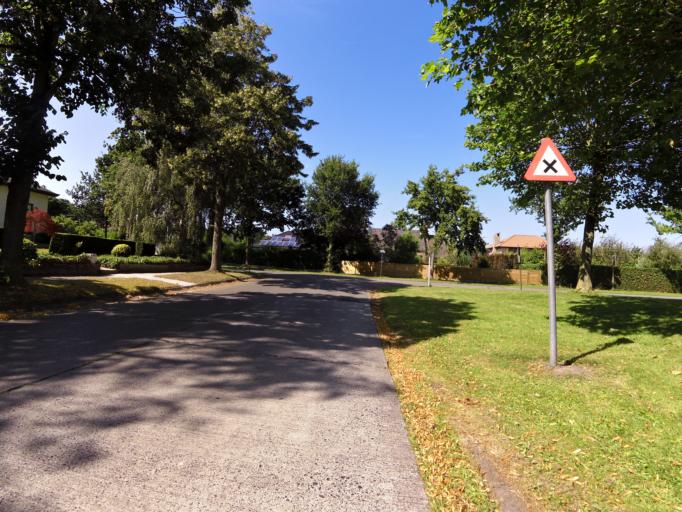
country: BE
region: Flanders
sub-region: Provincie West-Vlaanderen
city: Brugge
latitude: 51.2078
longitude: 3.1846
